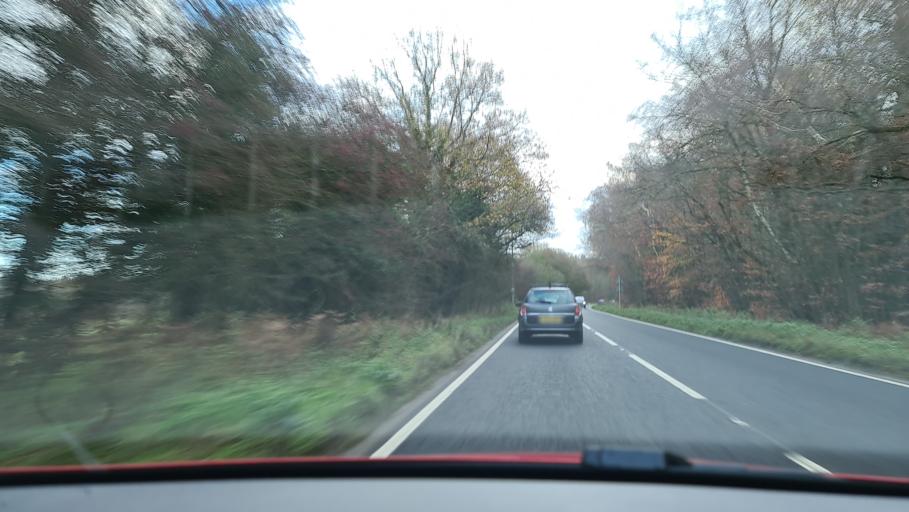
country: GB
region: England
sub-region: Buckinghamshire
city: Amersham
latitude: 51.6616
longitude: -0.6695
